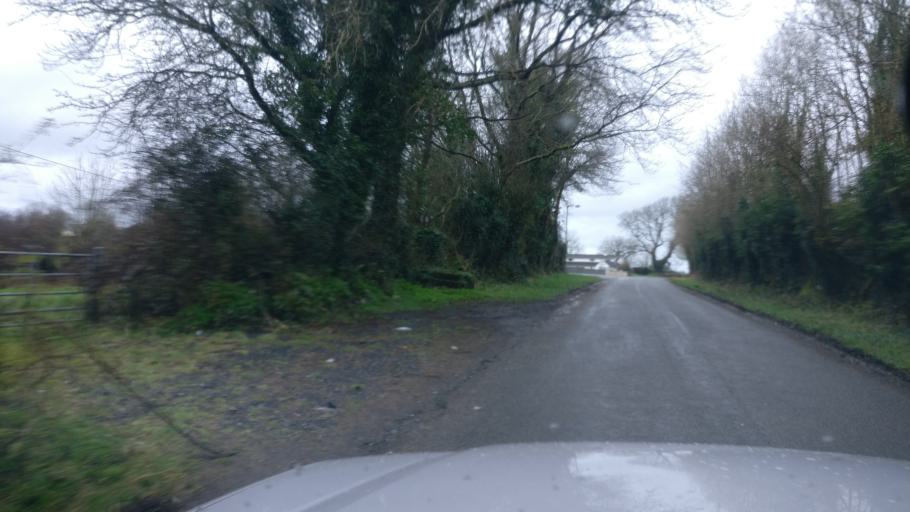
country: IE
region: Connaught
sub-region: County Galway
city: Ballinasloe
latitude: 53.2620
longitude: -8.3563
